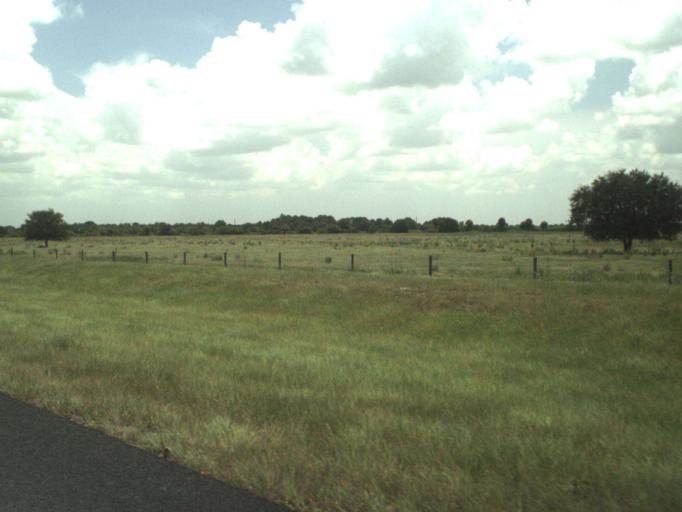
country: US
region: Florida
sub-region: Okeechobee County
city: Cypress Quarters
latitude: 27.3511
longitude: -80.6347
